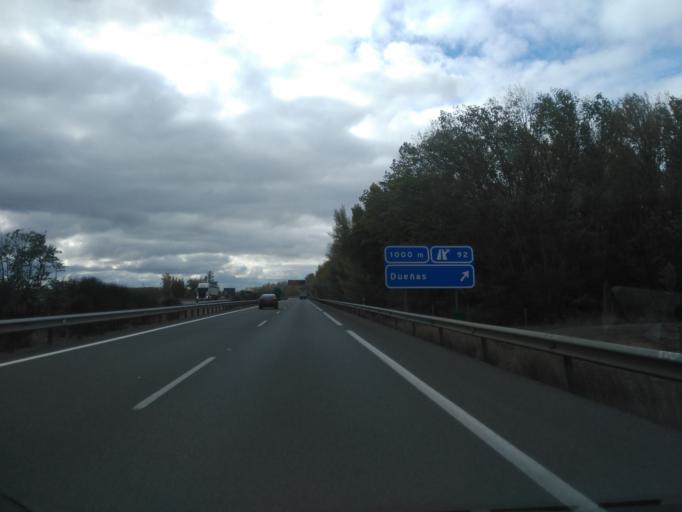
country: ES
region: Castille and Leon
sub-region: Provincia de Palencia
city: Duenas
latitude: 41.8976
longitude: -4.5203
